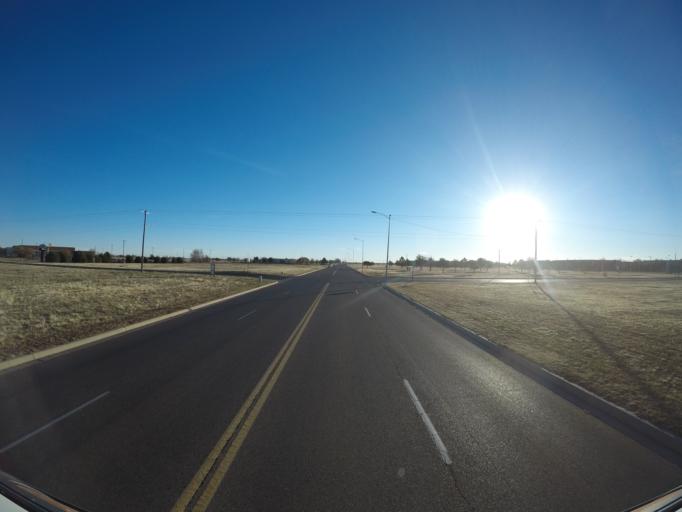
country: US
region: New Mexico
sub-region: Curry County
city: Clovis
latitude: 34.4049
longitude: -103.1688
